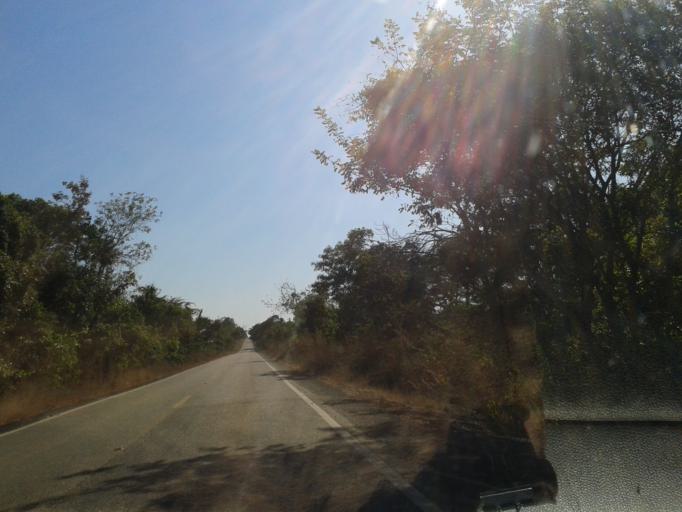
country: BR
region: Goias
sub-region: Mozarlandia
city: Mozarlandia
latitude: -14.6102
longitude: -50.5149
